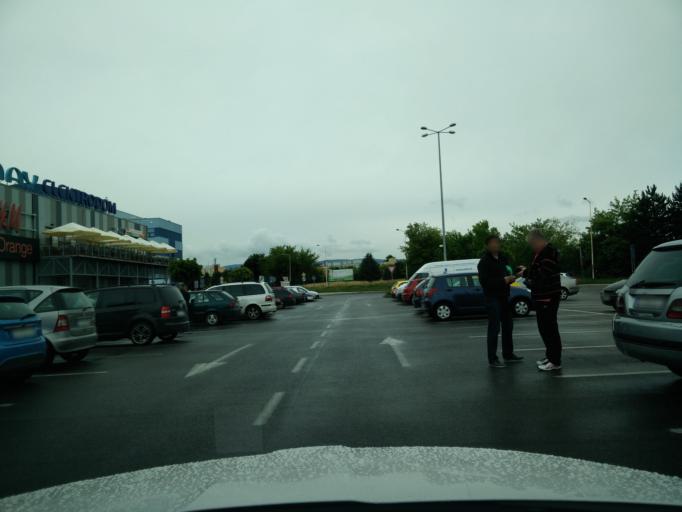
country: SK
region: Nitriansky
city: Prievidza
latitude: 48.7797
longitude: 18.6090
